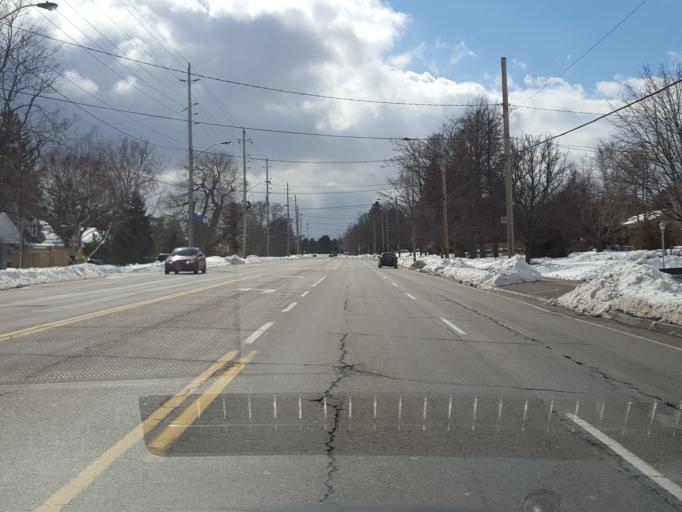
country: CA
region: Ontario
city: Hamilton
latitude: 43.2968
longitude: -79.8654
